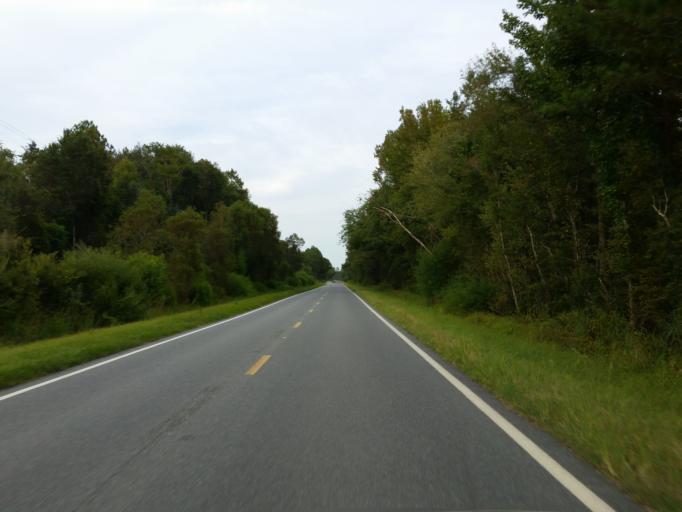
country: US
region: Georgia
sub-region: Echols County
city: Statenville
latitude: 30.5798
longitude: -83.1397
